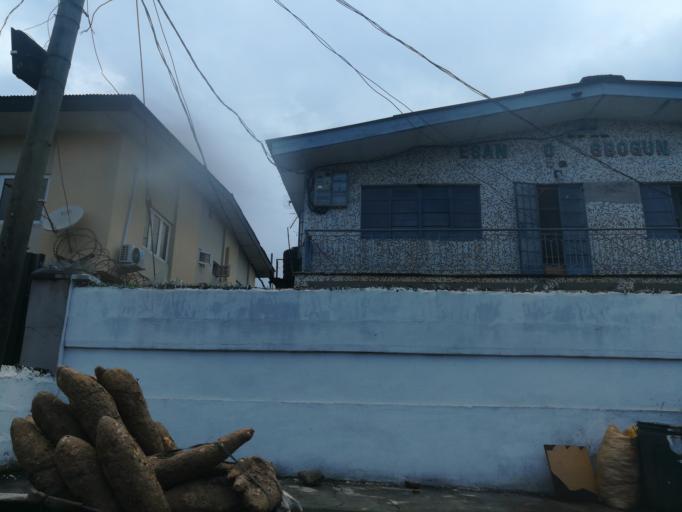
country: NG
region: Lagos
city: Ojota
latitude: 6.5631
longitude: 3.3701
